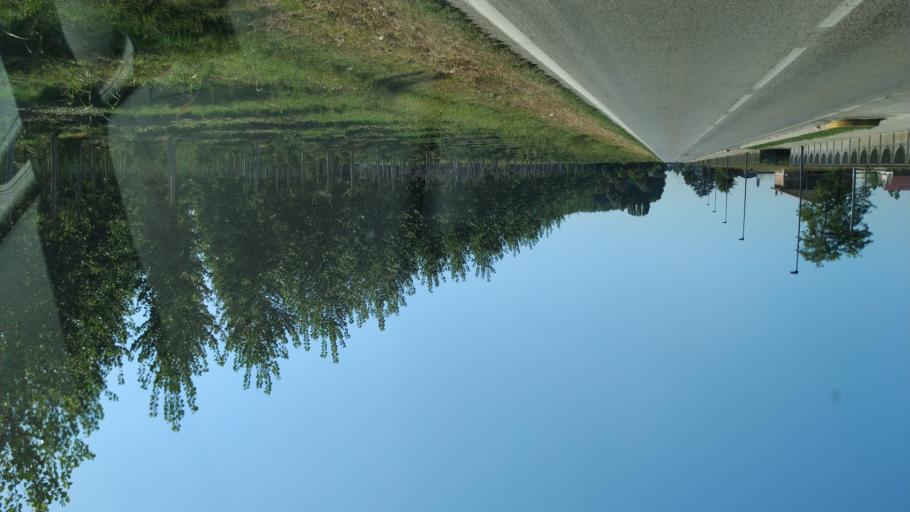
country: IT
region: Emilia-Romagna
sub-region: Provincia di Ferrara
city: Mirabello
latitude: 44.8151
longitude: 11.4432
